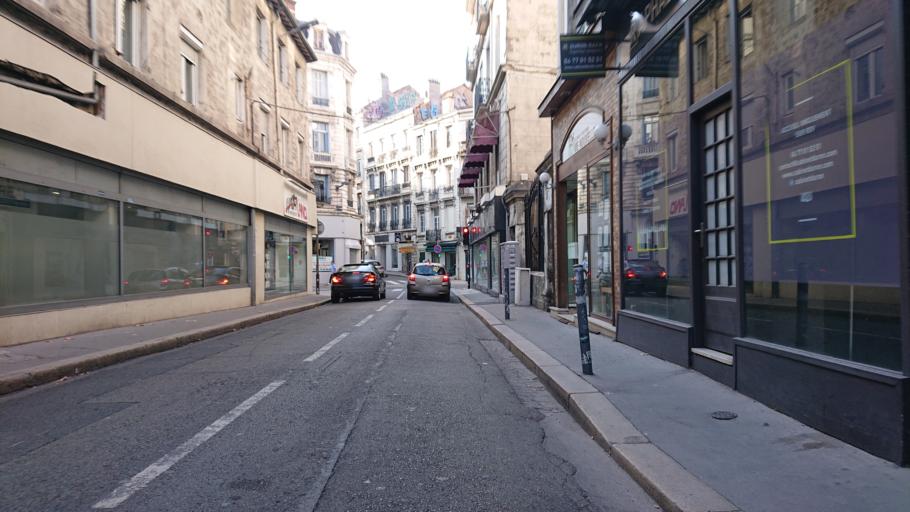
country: FR
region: Rhone-Alpes
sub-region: Departement de la Loire
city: Saint-Etienne
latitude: 45.4327
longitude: 4.3893
